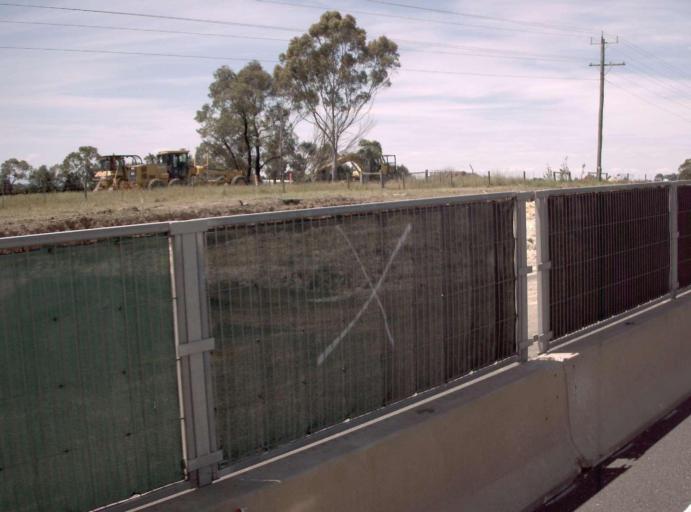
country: AU
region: Victoria
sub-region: Latrobe
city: Traralgon
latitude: -38.1872
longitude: 146.5818
